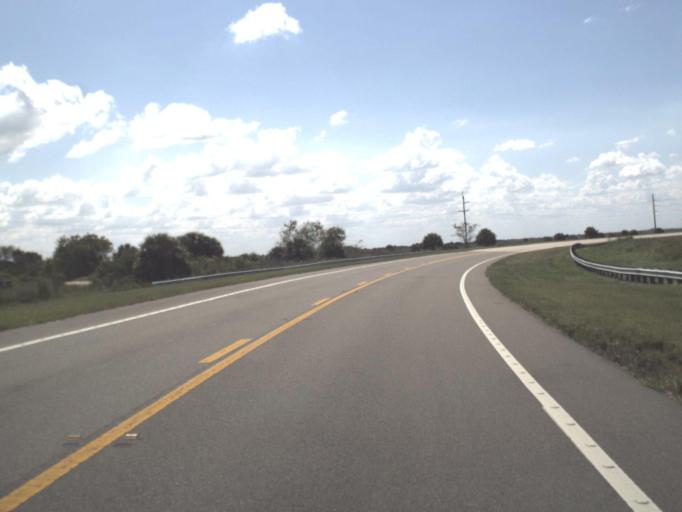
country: US
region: Florida
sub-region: Glades County
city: Moore Haven
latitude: 26.8134
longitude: -81.2047
